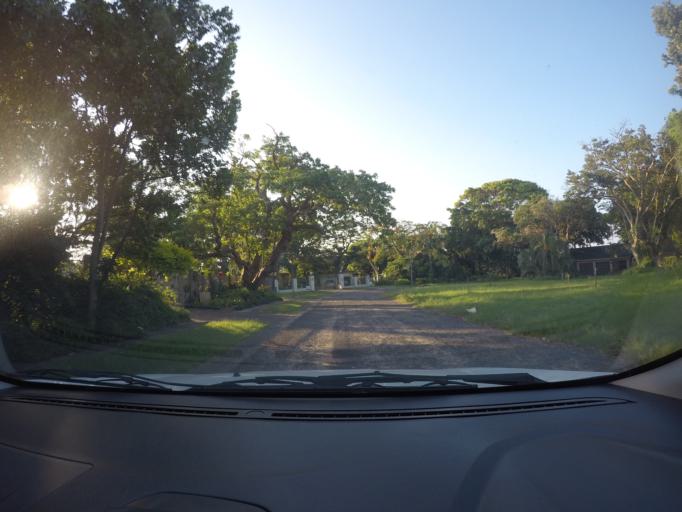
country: ZA
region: KwaZulu-Natal
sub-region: uThungulu District Municipality
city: Richards Bay
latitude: -28.7849
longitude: 32.0907
